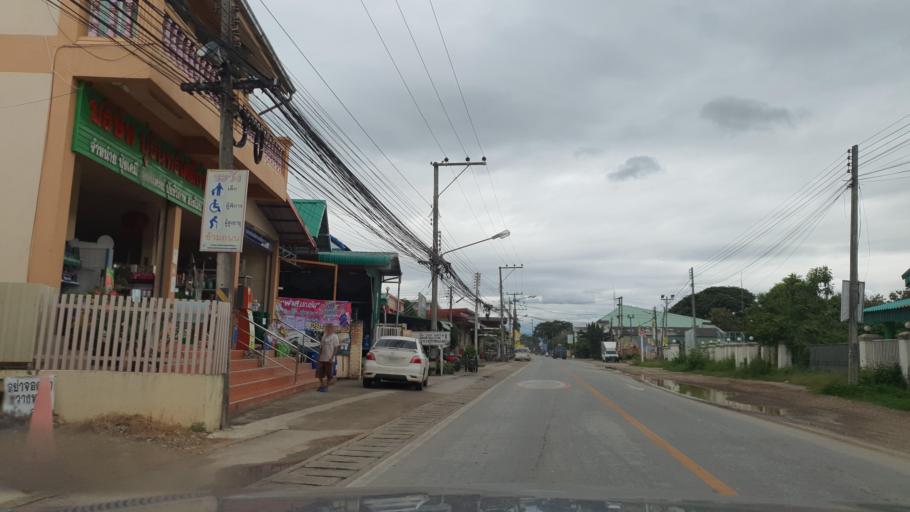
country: TH
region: Chiang Mai
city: San Pa Tong
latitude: 18.6164
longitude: 98.9517
